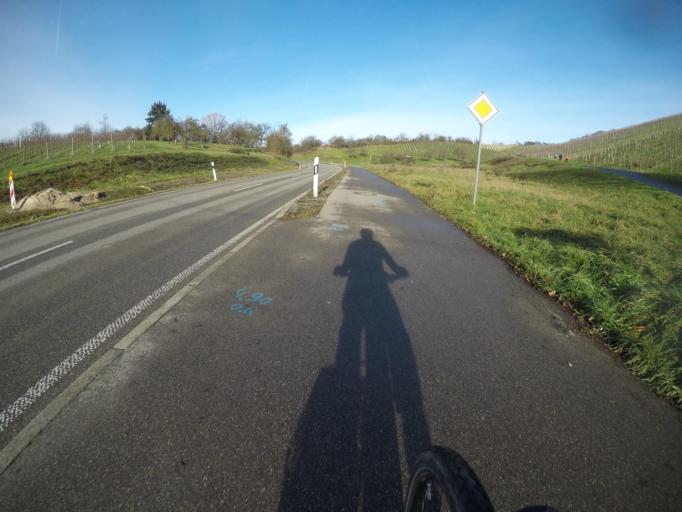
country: DE
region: Baden-Wuerttemberg
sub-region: Regierungsbezirk Stuttgart
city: Korb
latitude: 48.8487
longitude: 9.3567
